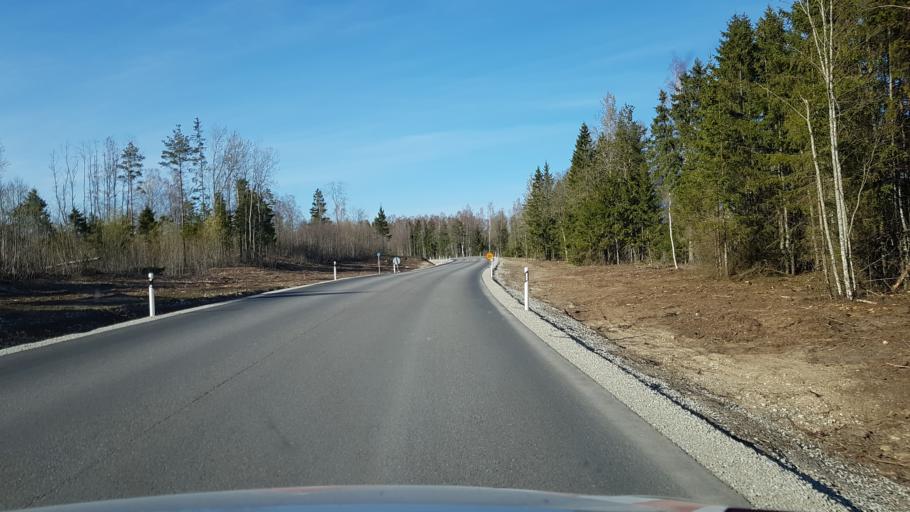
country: EE
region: Laeaene-Virumaa
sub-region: Vinni vald
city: Vinni
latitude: 59.1170
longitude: 26.6173
